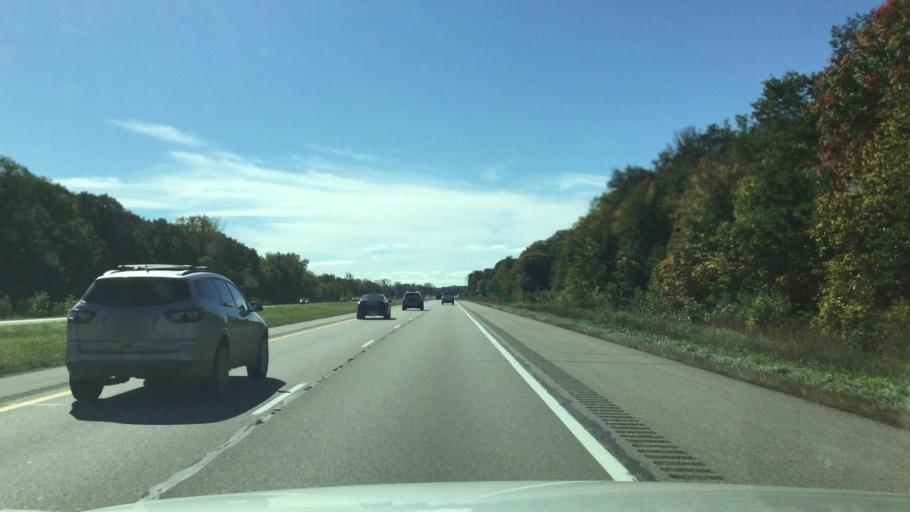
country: US
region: Michigan
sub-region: Washtenaw County
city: Ypsilanti
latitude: 42.3343
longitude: -83.6159
